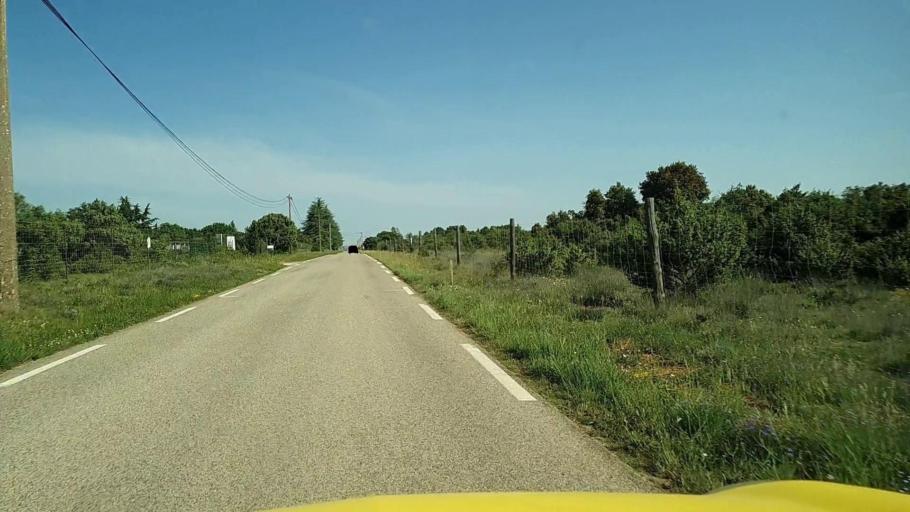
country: FR
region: Languedoc-Roussillon
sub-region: Departement du Gard
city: Montaren-et-Saint-Mediers
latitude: 44.1183
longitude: 4.3701
